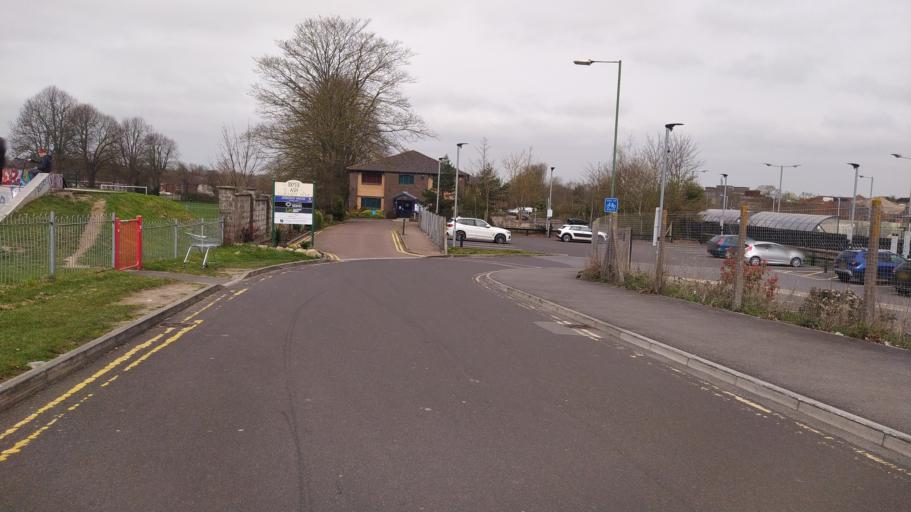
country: GB
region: England
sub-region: Wiltshire
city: Trowbridge
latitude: 51.3196
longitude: -2.2146
